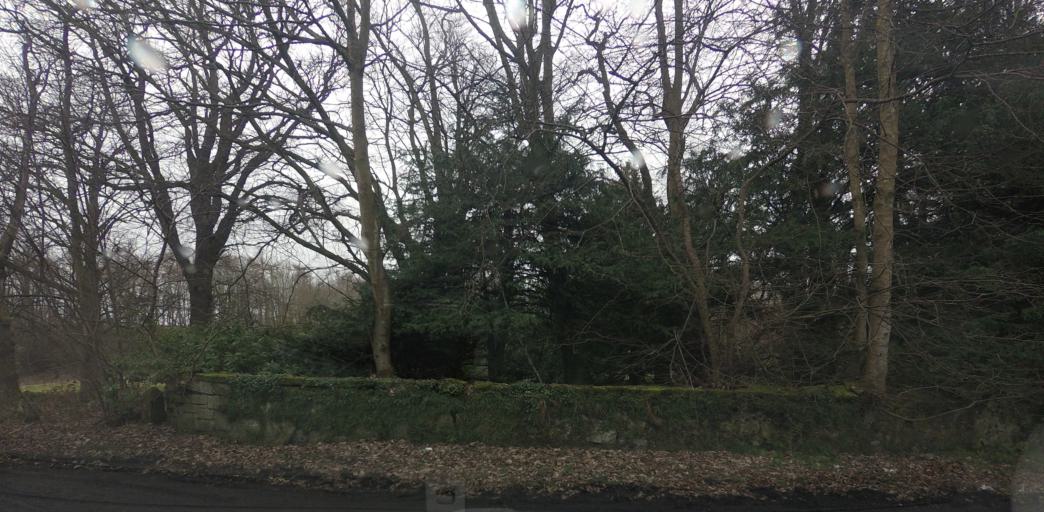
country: GB
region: Scotland
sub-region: Fife
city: Rosyth
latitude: 55.9950
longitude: -3.4434
